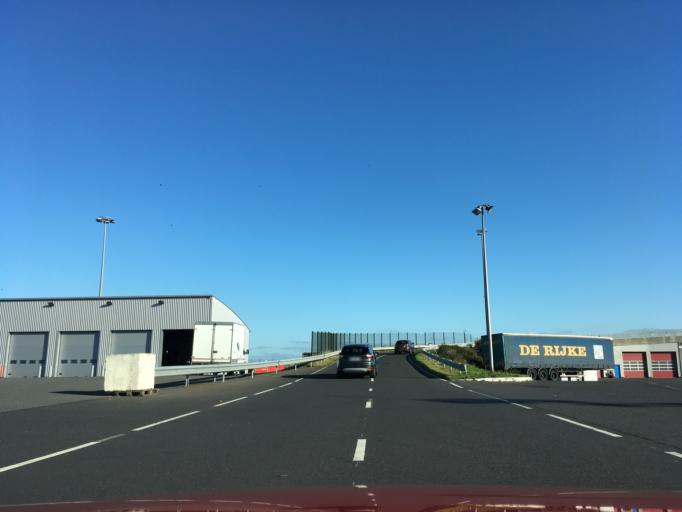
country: FR
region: Lower Normandy
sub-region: Departement du Calvados
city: Ouistreham
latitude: 49.2908
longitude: -0.2491
